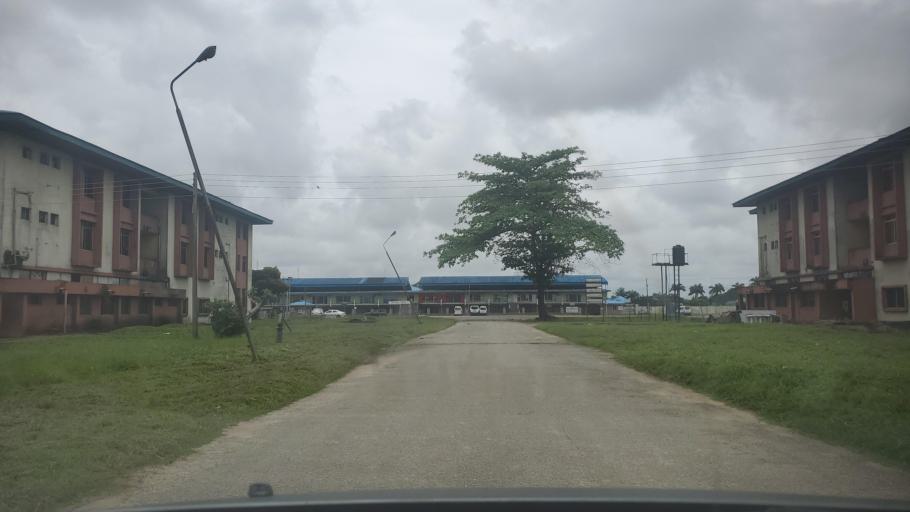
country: NG
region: Rivers
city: Emuoha
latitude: 4.8995
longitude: 6.9226
